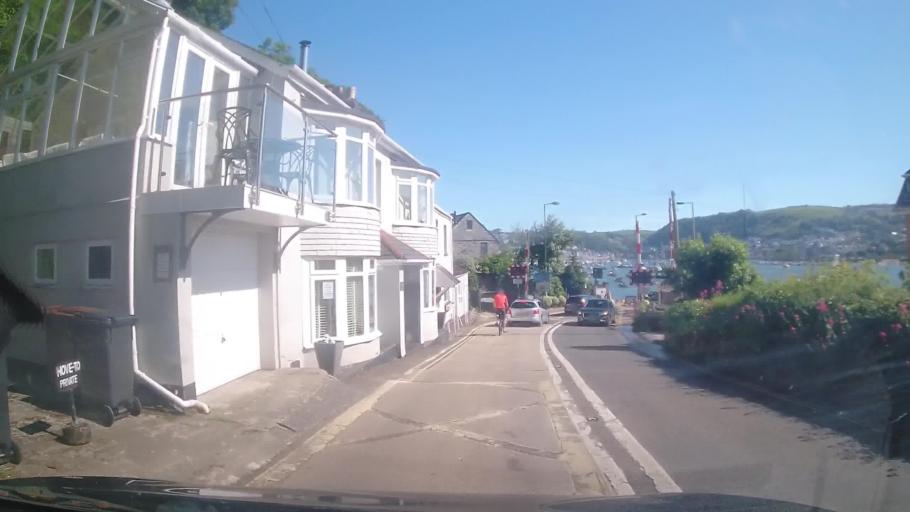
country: GB
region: England
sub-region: Devon
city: Dartmouth
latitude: 50.3605
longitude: -3.5731
